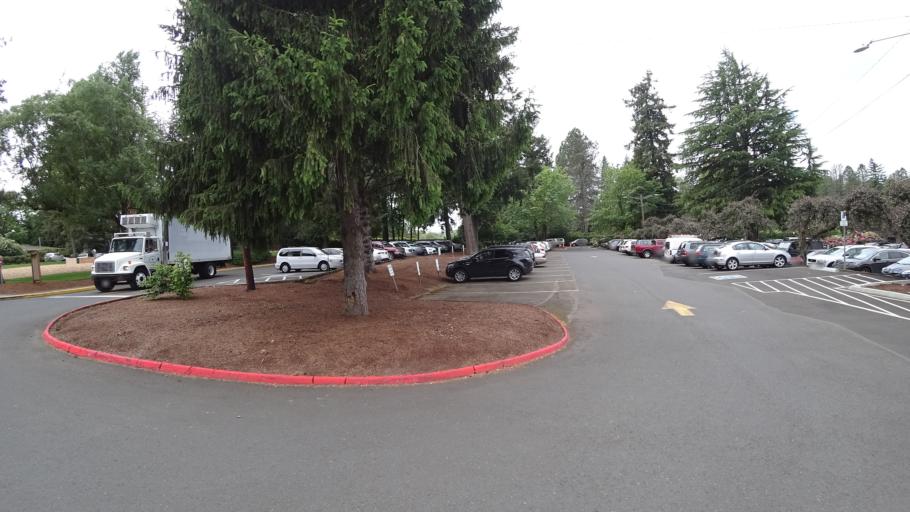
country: US
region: Oregon
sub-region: Washington County
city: Raleigh Hills
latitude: 45.4743
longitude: -122.7564
